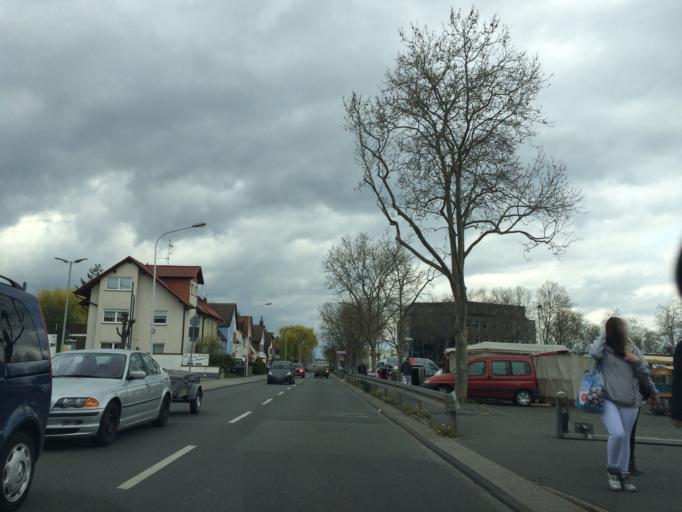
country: DE
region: Hesse
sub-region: Regierungsbezirk Darmstadt
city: Darmstadt
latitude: 49.8826
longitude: 8.6432
